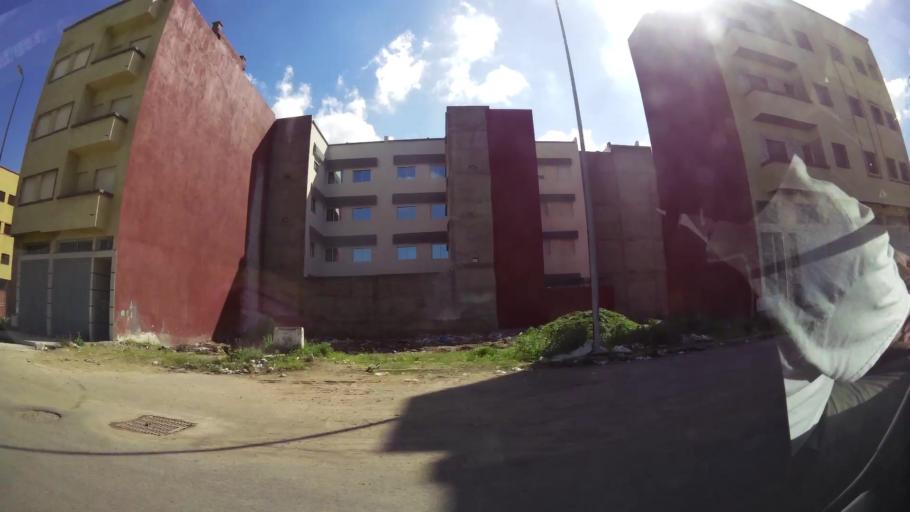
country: MA
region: Grand Casablanca
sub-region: Mediouna
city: Mediouna
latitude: 33.4593
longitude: -7.5140
